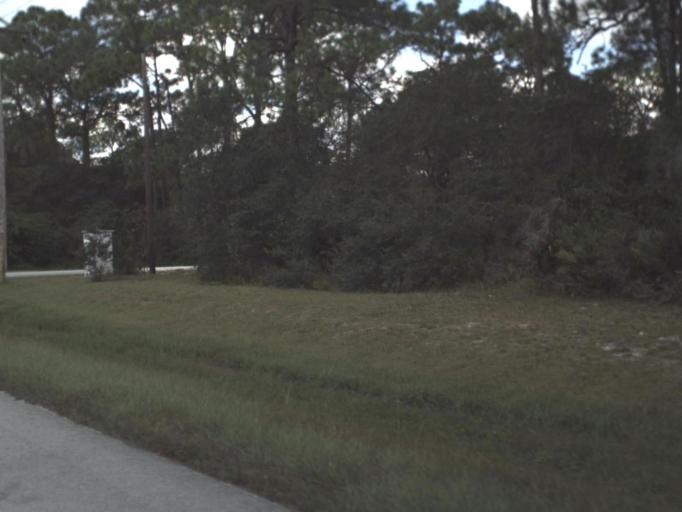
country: US
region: Florida
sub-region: Highlands County
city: Sebring
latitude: 27.4125
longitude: -81.4623
